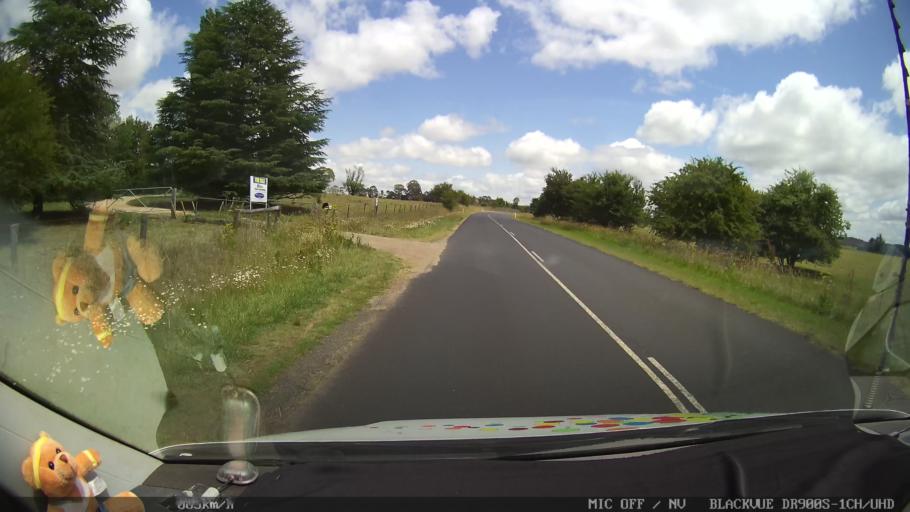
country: AU
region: New South Wales
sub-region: Glen Innes Severn
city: Glen Innes
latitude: -29.7042
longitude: 151.7196
